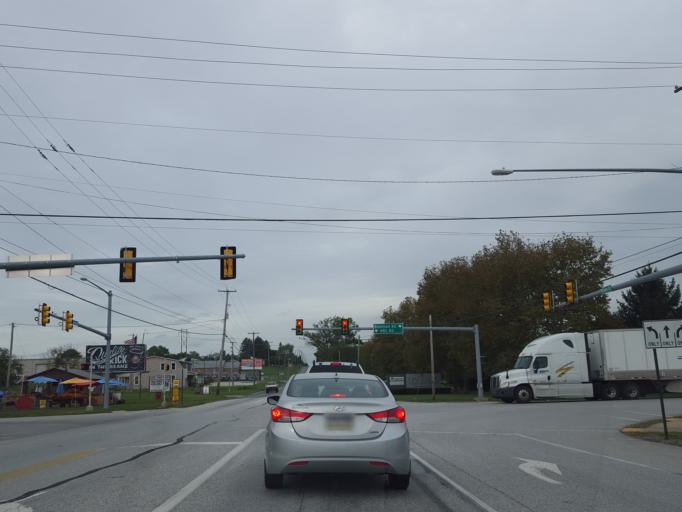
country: US
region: Pennsylvania
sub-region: York County
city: Weigelstown
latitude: 39.9286
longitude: -76.8370
